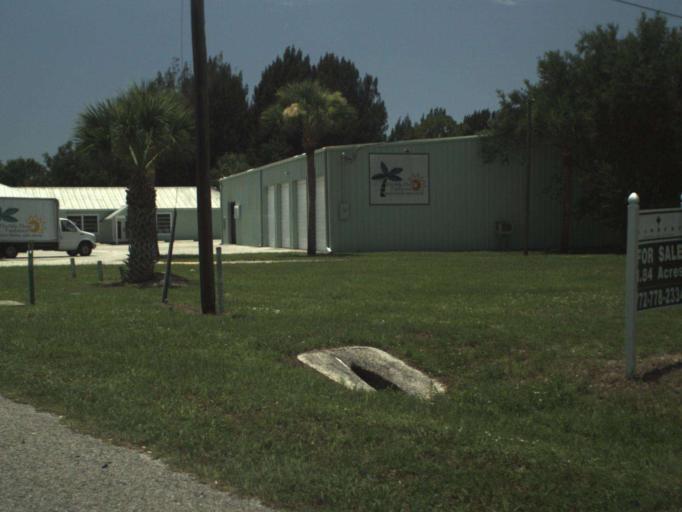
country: US
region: Florida
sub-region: Indian River County
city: Wabasso Beach
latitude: 27.7646
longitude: -80.4426
